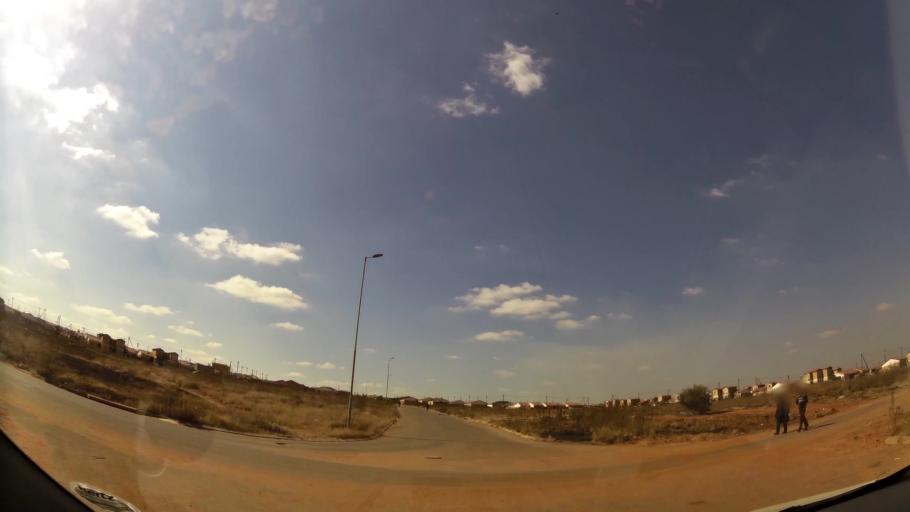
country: ZA
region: Gauteng
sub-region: West Rand District Municipality
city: Randfontein
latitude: -26.1712
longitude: 27.7718
